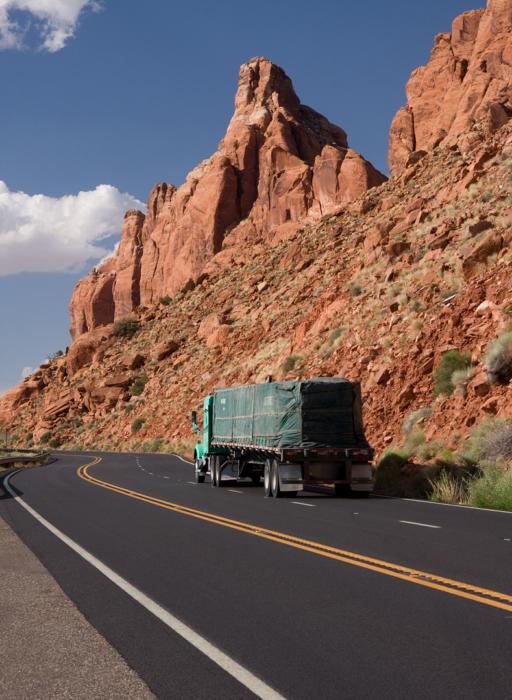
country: US
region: Arizona
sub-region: Coconino County
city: LeChee
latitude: 36.6612
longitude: -111.6330
